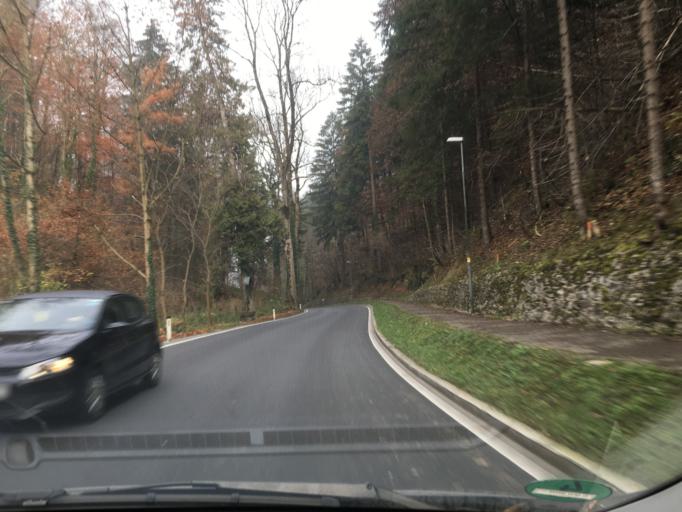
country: AT
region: Vorarlberg
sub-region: Politischer Bezirk Feldkirch
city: Gotzis
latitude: 47.3280
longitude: 9.6452
